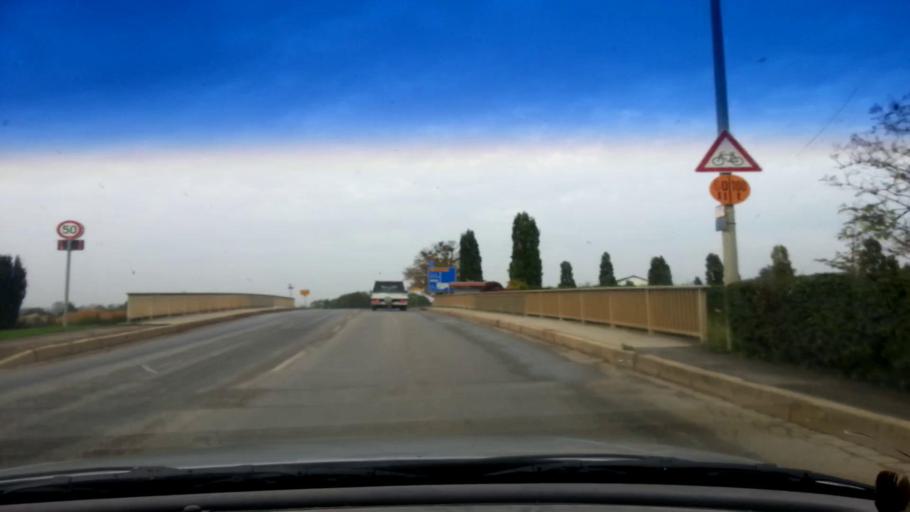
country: DE
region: Bavaria
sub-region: Upper Franconia
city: Breitengussbach
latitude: 49.9739
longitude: 10.8880
